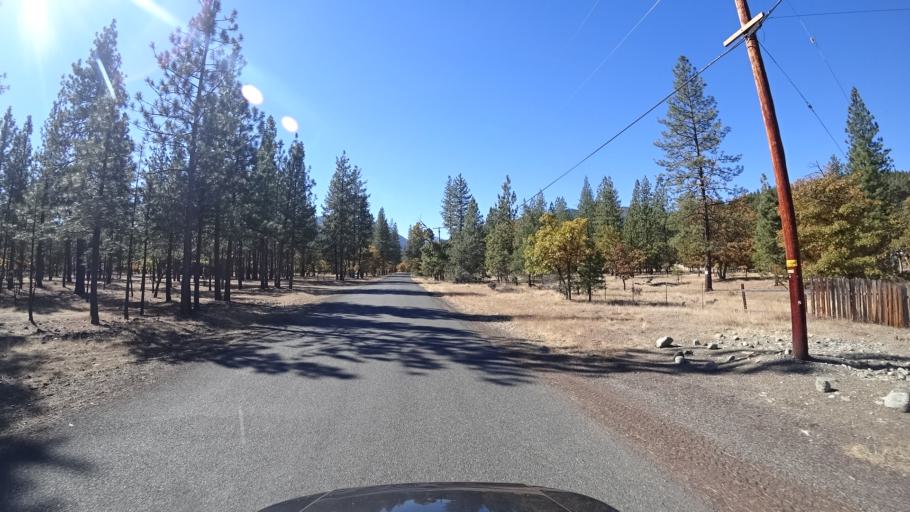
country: US
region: California
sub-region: Siskiyou County
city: Yreka
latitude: 41.5410
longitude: -122.9480
